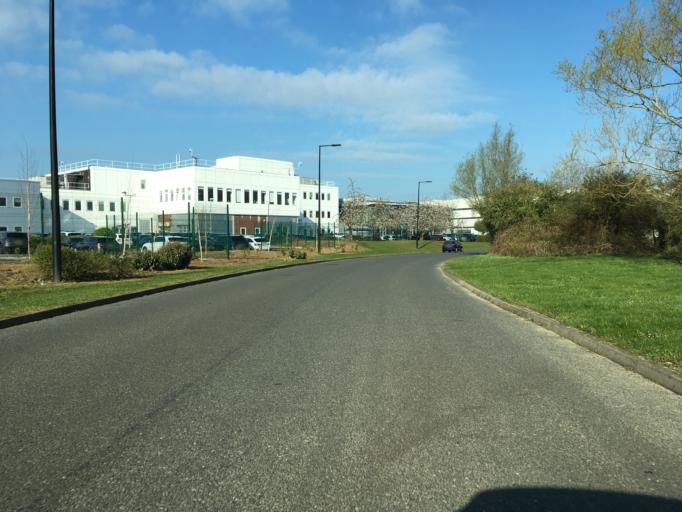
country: GB
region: England
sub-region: Milton Keynes
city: Newport Pagnell
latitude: 52.0701
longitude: -0.7355
